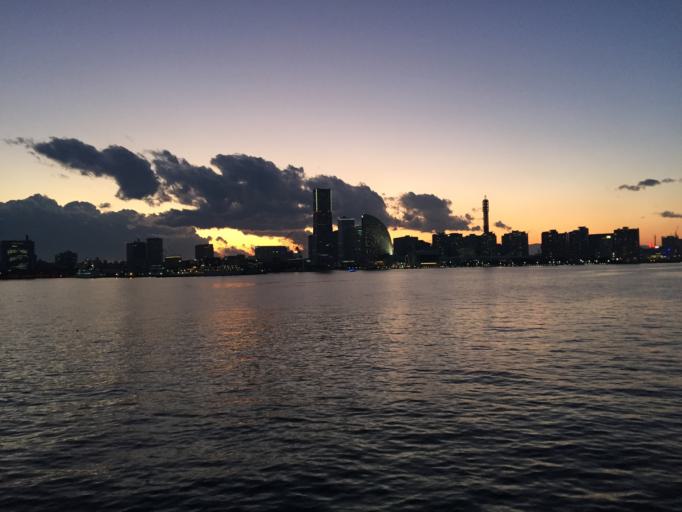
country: JP
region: Kanagawa
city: Yokohama
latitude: 35.4610
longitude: 139.6540
